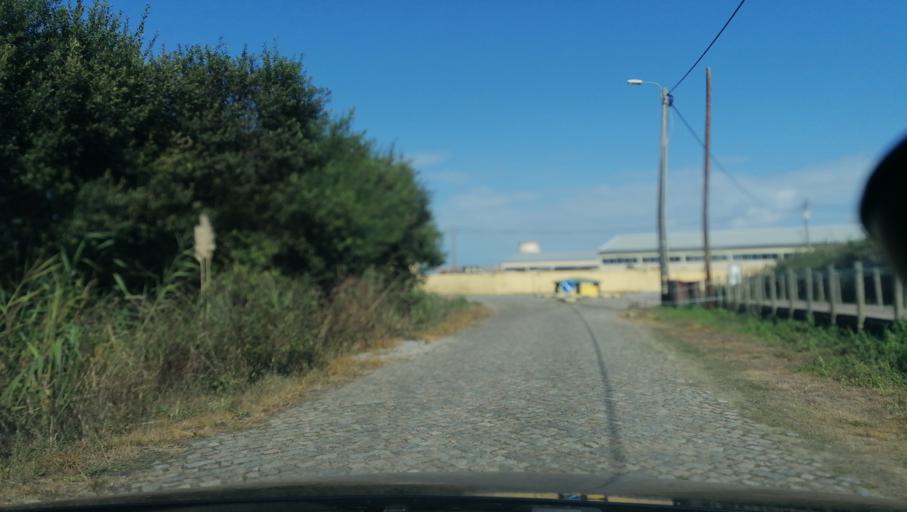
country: PT
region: Aveiro
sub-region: Ovar
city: Esmoriz
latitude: 40.9743
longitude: -8.6413
